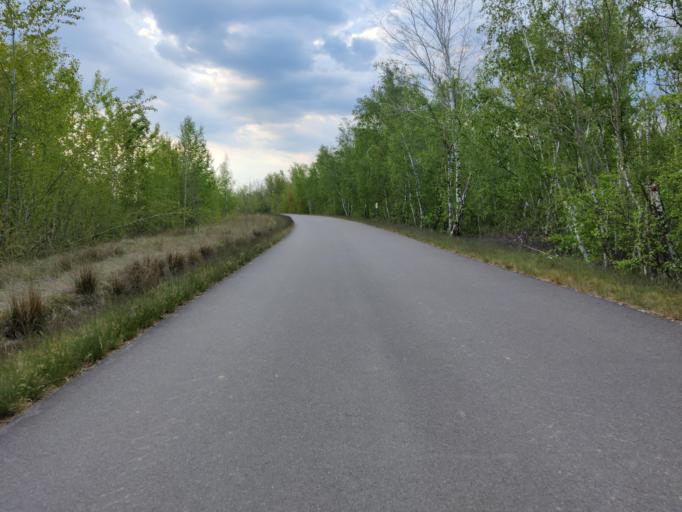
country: DE
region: Saxony
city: Rotha
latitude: 51.2106
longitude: 12.4429
